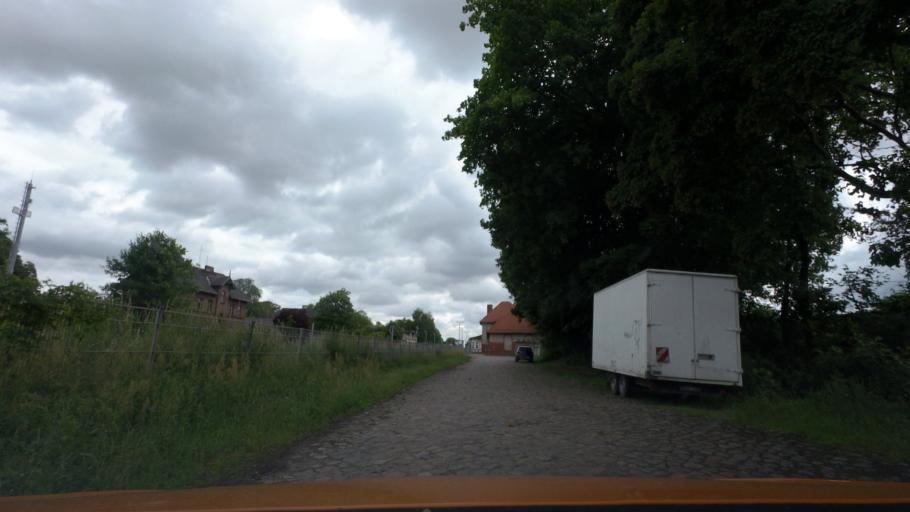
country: DE
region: Brandenburg
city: Neutrebbin
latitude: 52.6766
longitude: 14.2357
